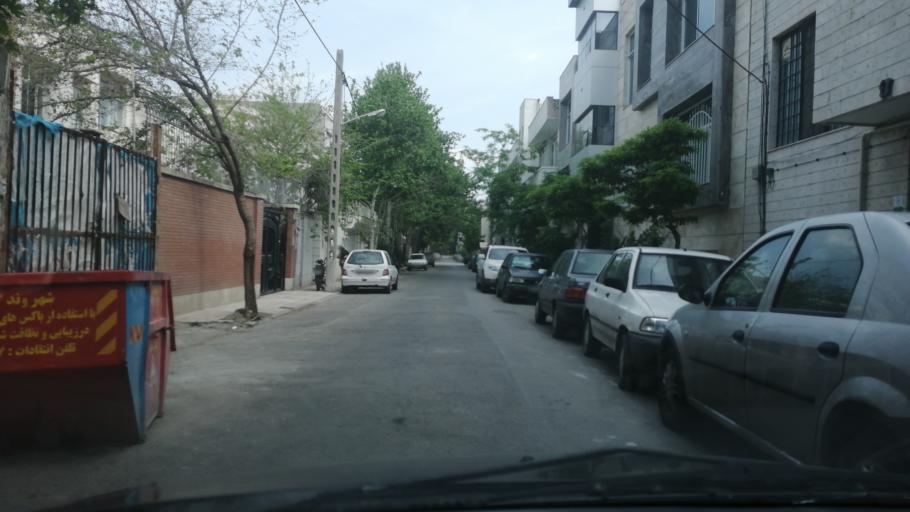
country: IR
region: Razavi Khorasan
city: Mashhad
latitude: 36.3081
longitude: 59.5540
